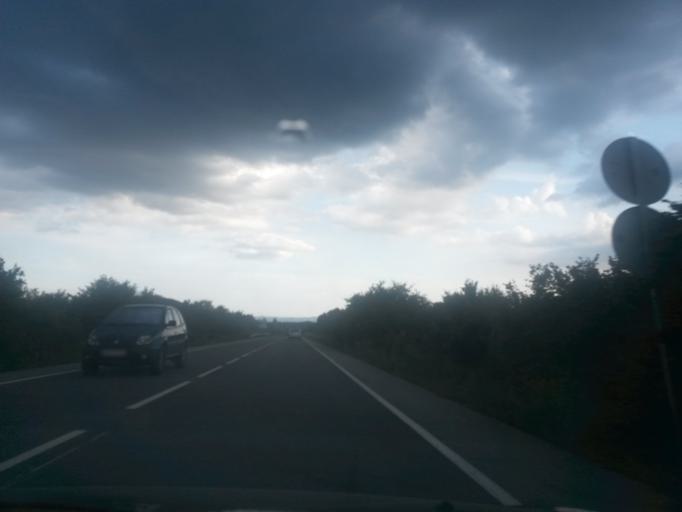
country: ES
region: Catalonia
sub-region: Provincia de Girona
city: Brunyola
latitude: 41.9168
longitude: 2.6562
